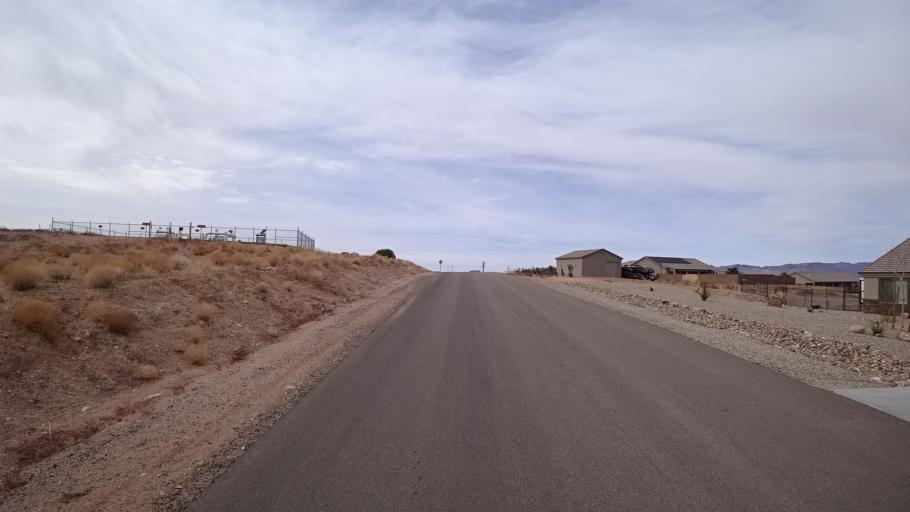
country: US
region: Arizona
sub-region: Mohave County
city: Kingman
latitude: 35.1813
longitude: -113.9767
